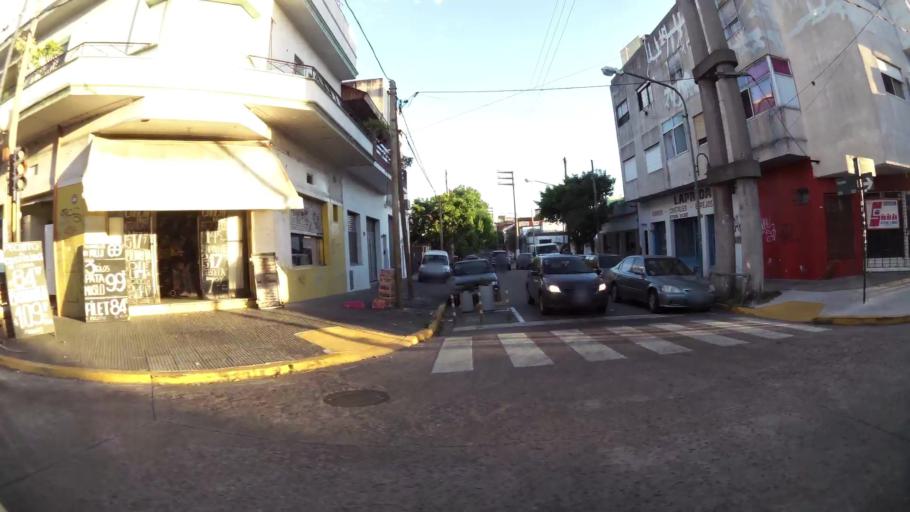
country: AR
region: Buenos Aires
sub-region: Partido de General San Martin
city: General San Martin
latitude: -34.5510
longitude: -58.5110
